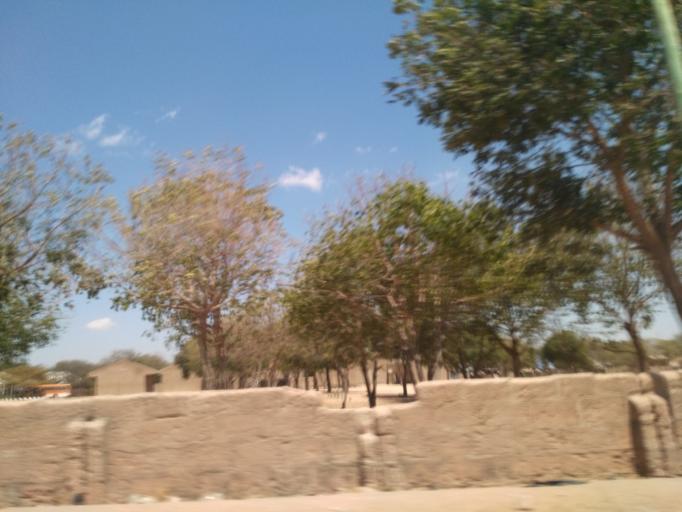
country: TZ
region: Dodoma
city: Kisasa
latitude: -6.1684
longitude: 35.7710
